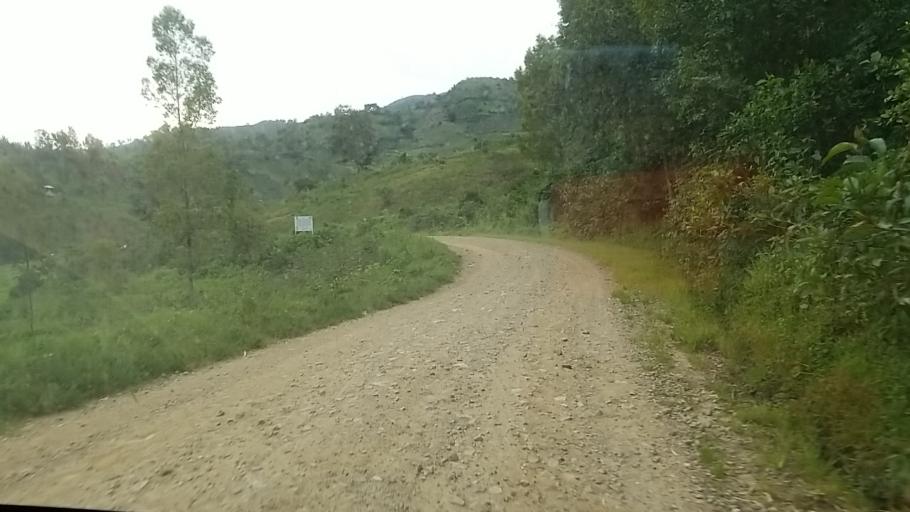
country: CD
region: Nord Kivu
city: Sake
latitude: -1.9599
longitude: 28.9177
